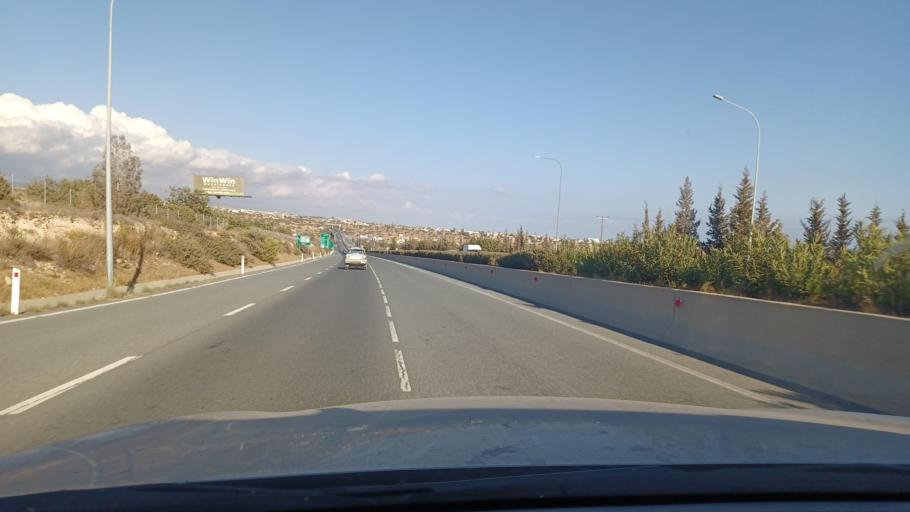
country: CY
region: Limassol
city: Erimi
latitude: 34.6811
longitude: 32.8978
